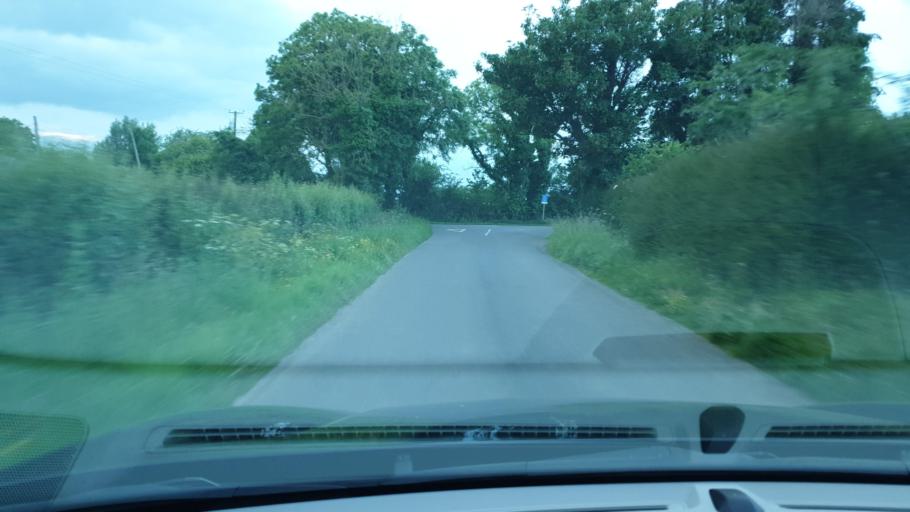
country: IE
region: Leinster
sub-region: An Mhi
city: Ashbourne
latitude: 53.5228
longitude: -6.3872
